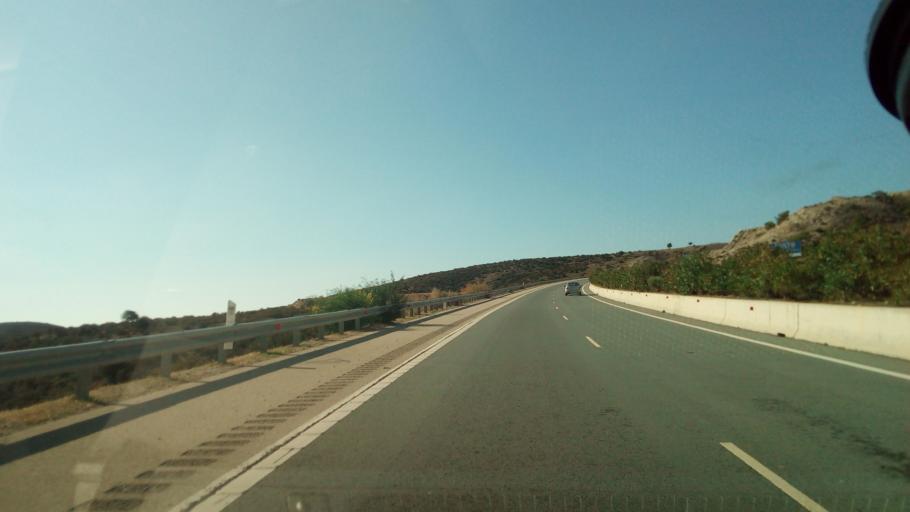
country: CY
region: Limassol
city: Pissouri
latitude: 34.6695
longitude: 32.6569
